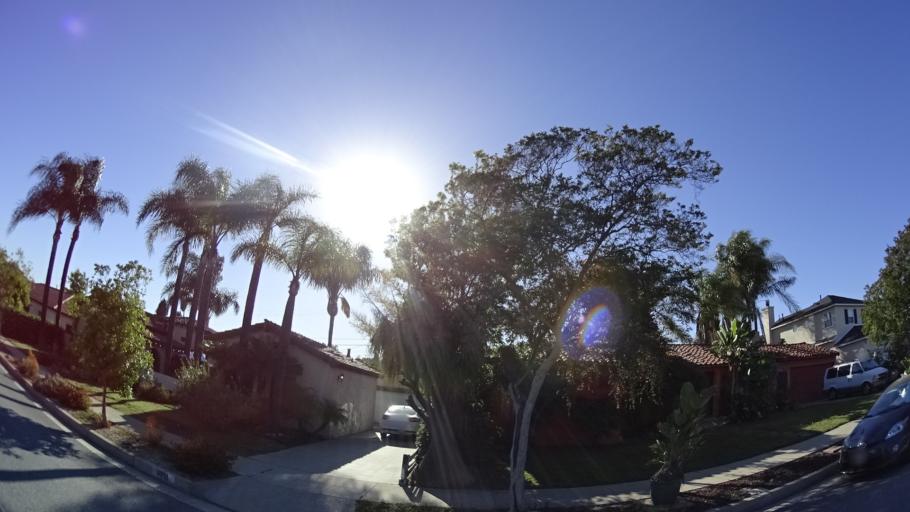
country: US
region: California
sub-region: Los Angeles County
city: Belvedere
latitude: 34.0668
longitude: -118.1597
